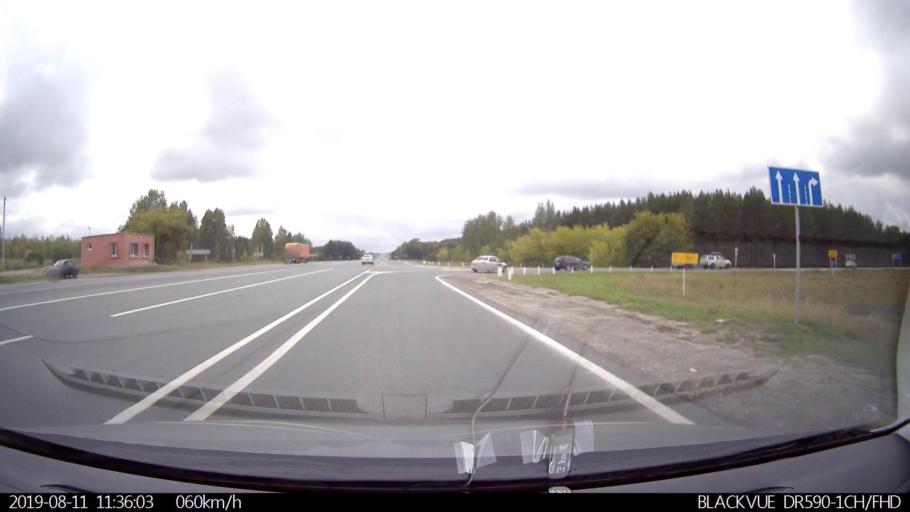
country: RU
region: Ulyanovsk
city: Silikatnyy
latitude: 54.0001
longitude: 48.2234
